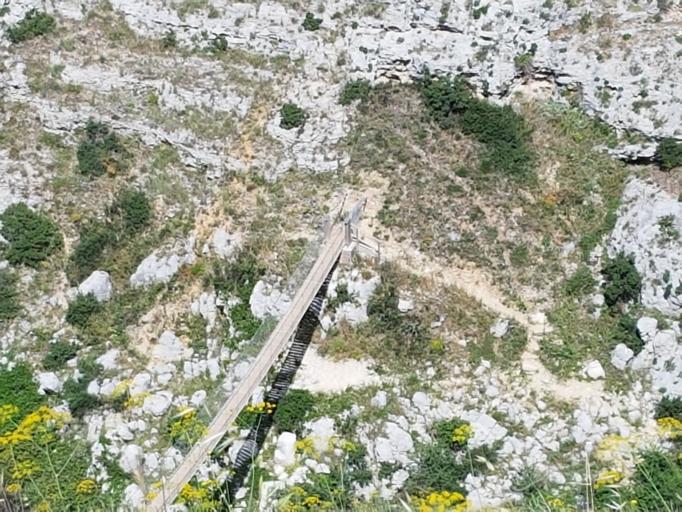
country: IT
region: Basilicate
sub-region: Provincia di Matera
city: Matera
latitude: 40.6653
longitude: 16.6158
